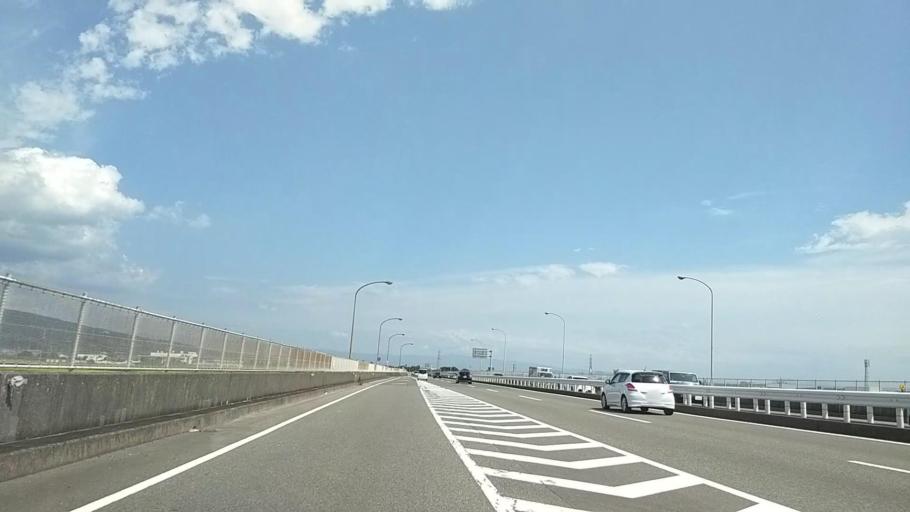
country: JP
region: Shizuoka
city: Fuji
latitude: 35.1486
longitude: 138.7168
